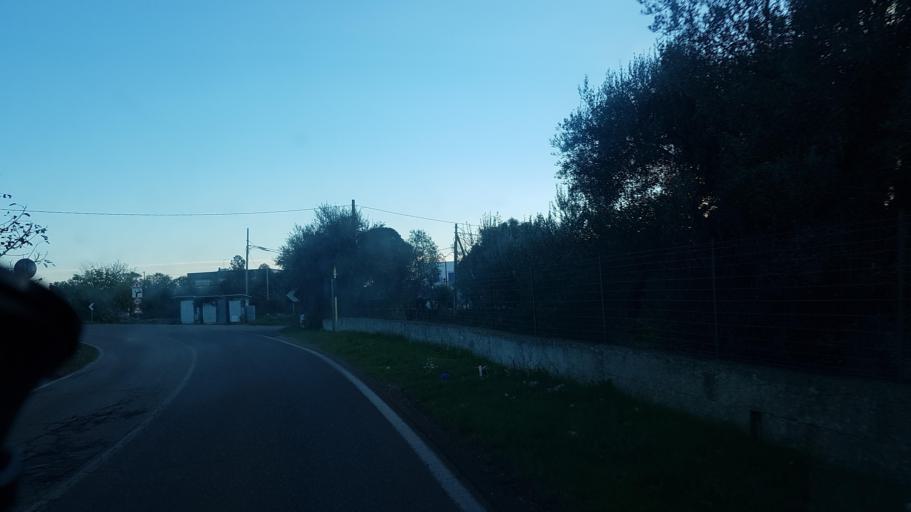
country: IT
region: Apulia
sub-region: Provincia di Brindisi
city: Ostuni
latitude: 40.6966
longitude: 17.5929
